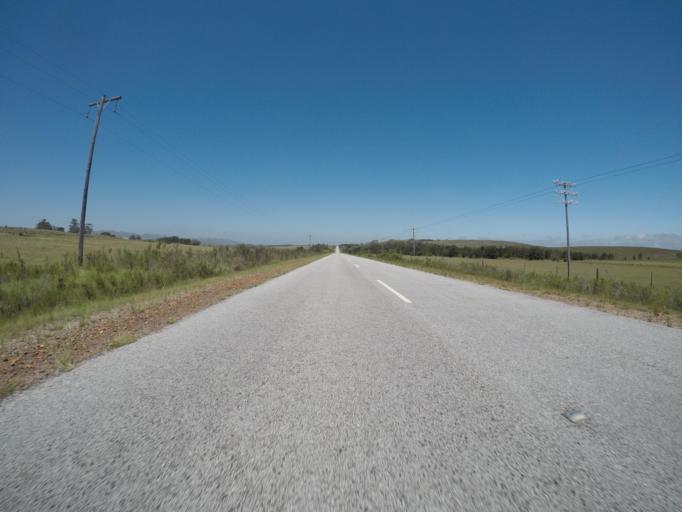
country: ZA
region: Eastern Cape
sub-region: Cacadu District Municipality
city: Kareedouw
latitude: -33.9765
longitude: 24.4929
